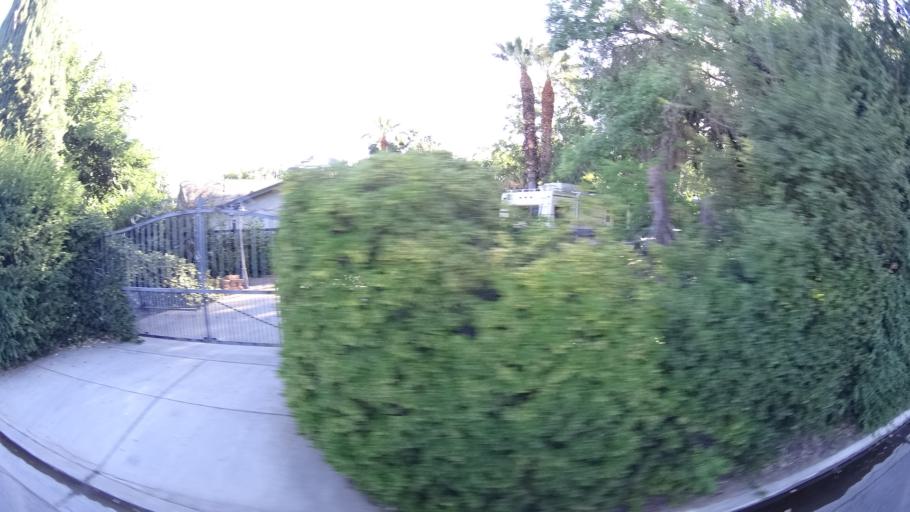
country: US
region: California
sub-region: Fresno County
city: Fresno
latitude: 36.7960
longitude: -119.8217
